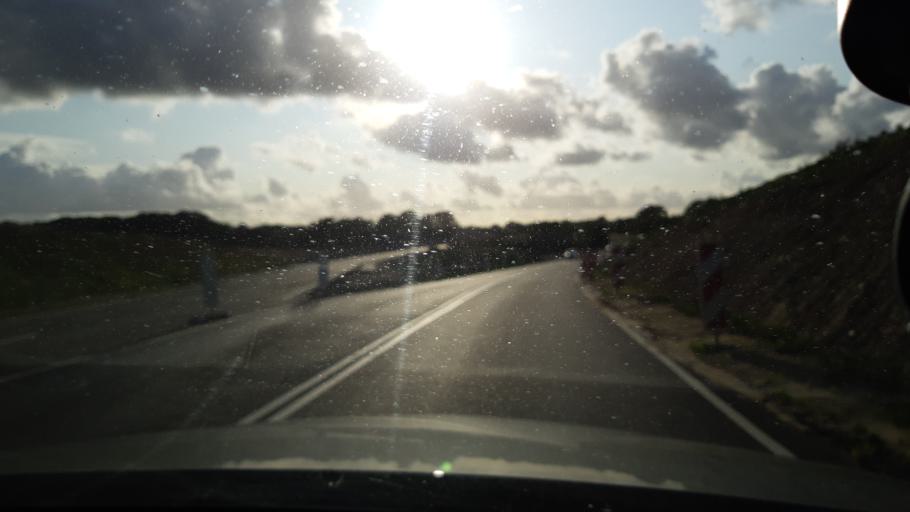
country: DK
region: Zealand
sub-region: Soro Kommune
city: Stenlille
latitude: 55.6587
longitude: 11.5727
